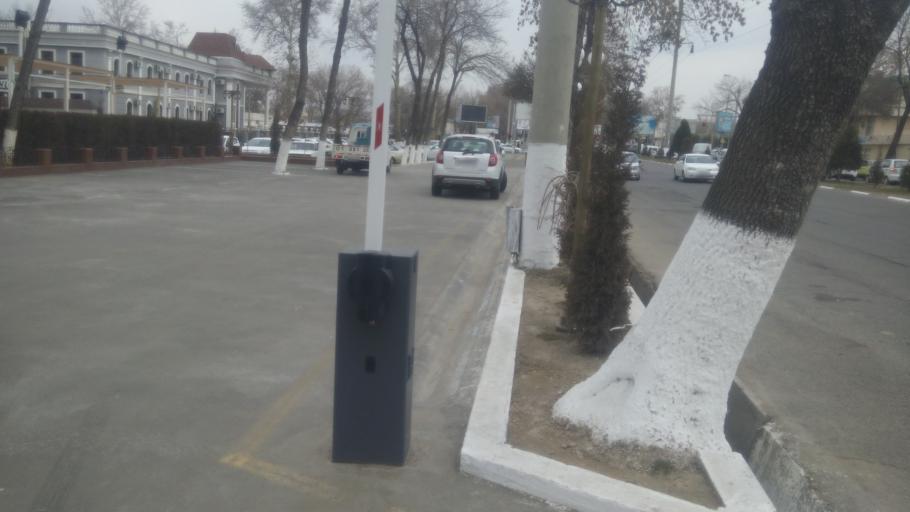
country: UZ
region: Toshkent Shahri
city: Tashkent
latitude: 41.3498
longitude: 69.2256
